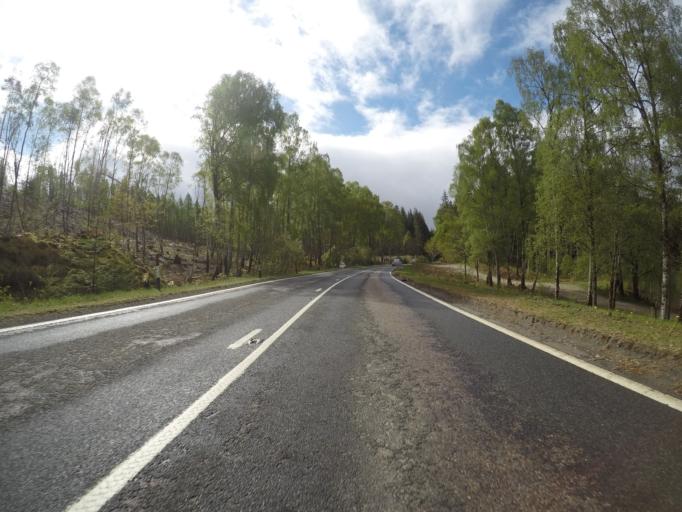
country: GB
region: Scotland
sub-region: Highland
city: Spean Bridge
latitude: 57.0707
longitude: -4.8312
